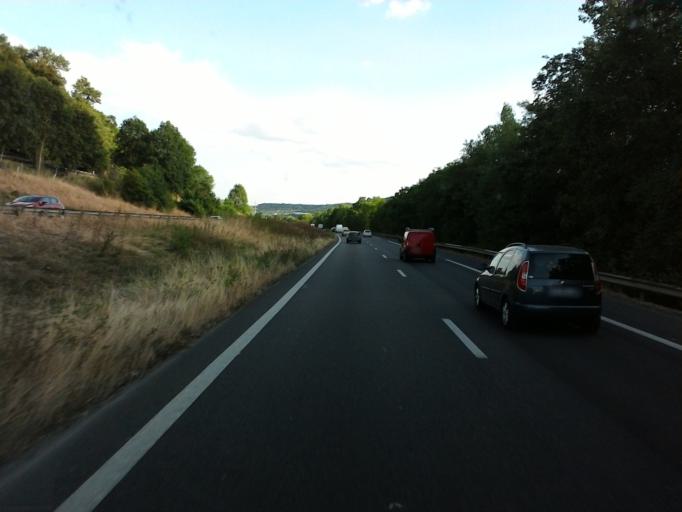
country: FR
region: Lorraine
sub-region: Departement de Meurthe-et-Moselle
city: Frouard
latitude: 48.7700
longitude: 6.1434
